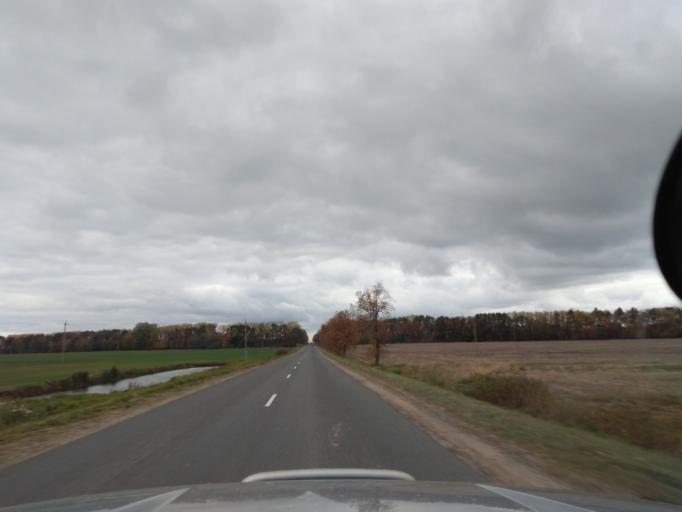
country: BY
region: Minsk
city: Slutsk
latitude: 53.2190
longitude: 27.3630
